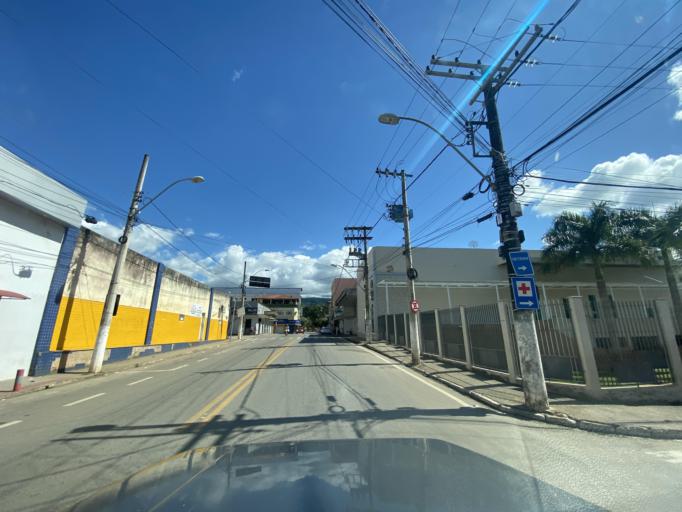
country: BR
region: Espirito Santo
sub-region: Alegre
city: Alegre
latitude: -20.7626
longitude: -41.5296
